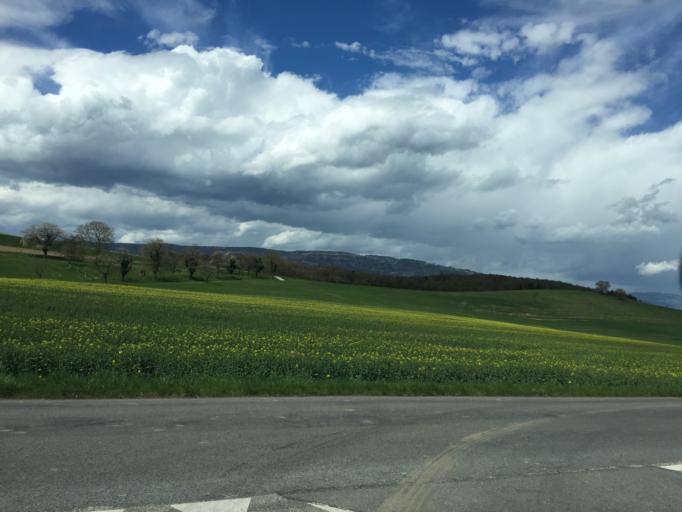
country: CH
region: Vaud
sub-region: Morges District
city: La Chaux
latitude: 46.6204
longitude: 6.4717
